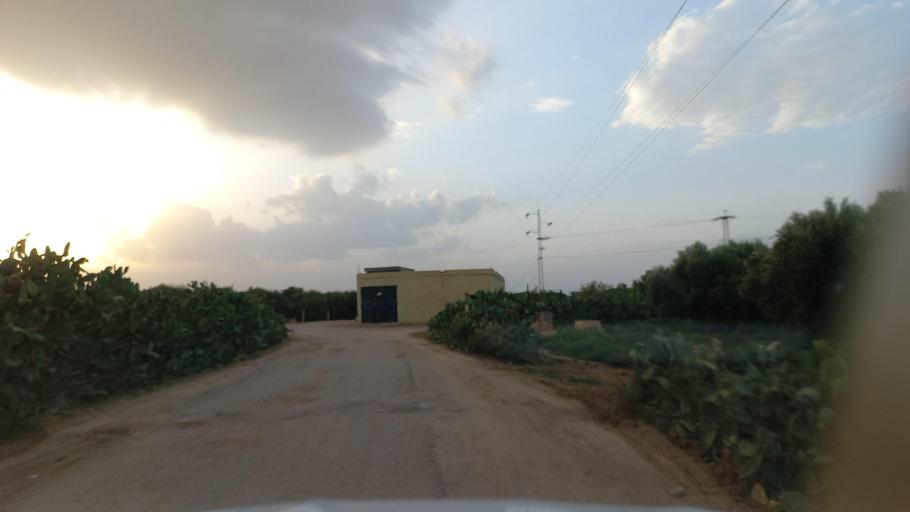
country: TN
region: Al Qasrayn
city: Kasserine
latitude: 35.2714
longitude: 9.0555
